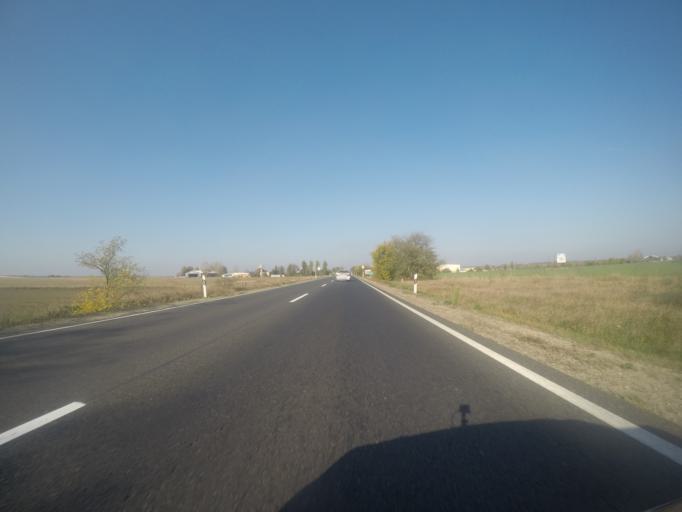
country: HU
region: Fejer
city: Baracs
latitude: 46.8922
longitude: 18.9211
